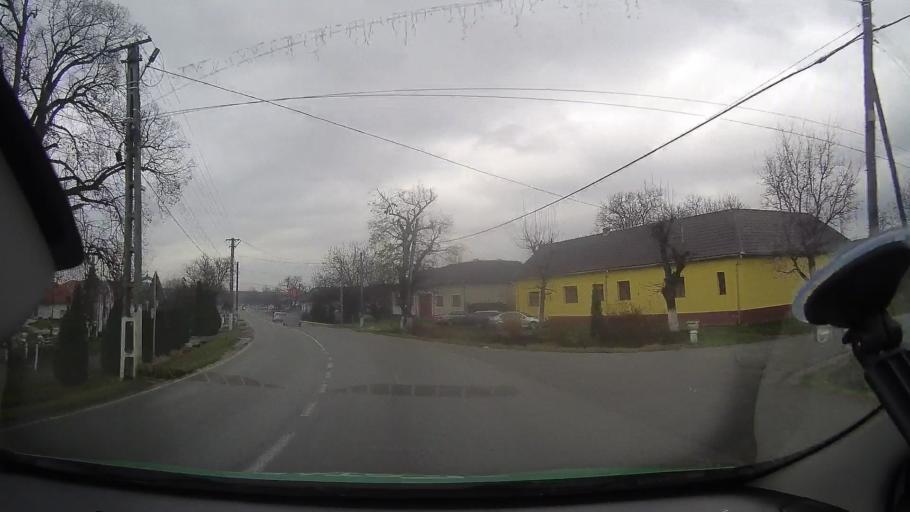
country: RO
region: Arad
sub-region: Comuna Almas
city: Almas
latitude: 46.2845
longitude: 22.2353
